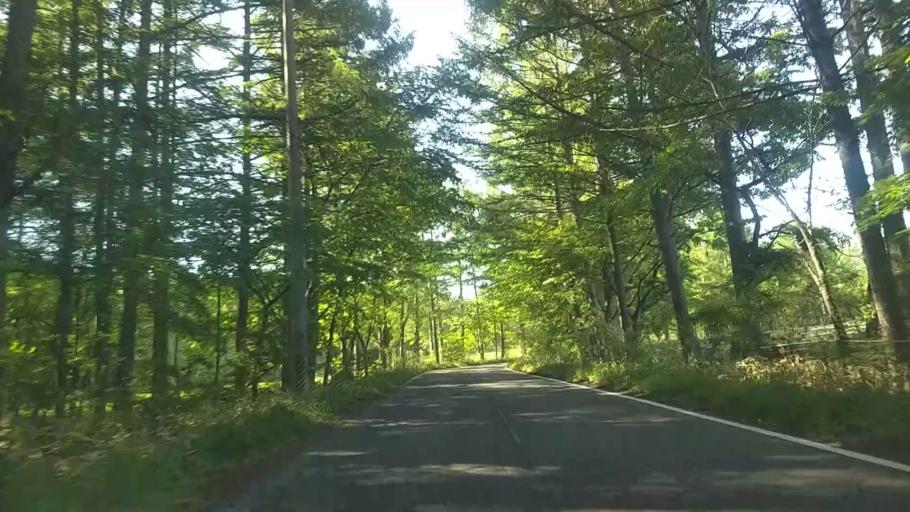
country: JP
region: Yamanashi
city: Nirasaki
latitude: 35.8902
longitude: 138.3505
